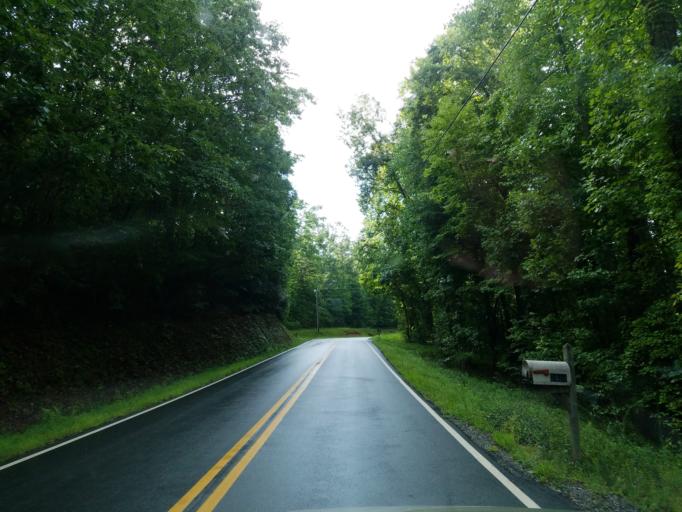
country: US
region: Georgia
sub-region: White County
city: Cleveland
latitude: 34.6288
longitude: -83.8668
